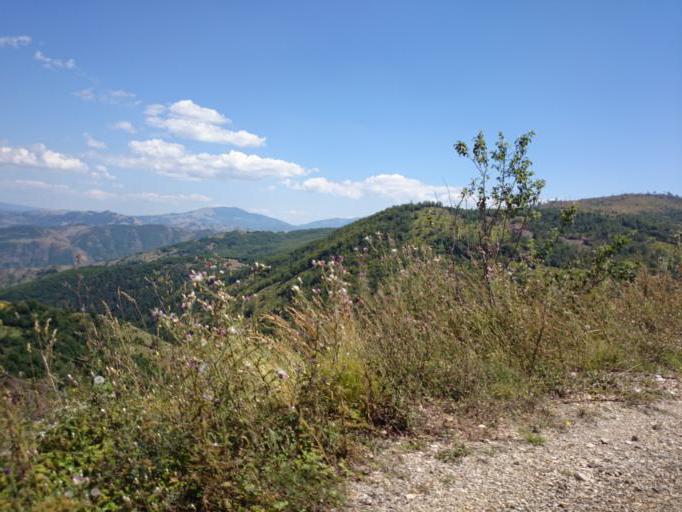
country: AL
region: Diber
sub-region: Rrethi i Bulqizes
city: Zerqan
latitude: 41.4308
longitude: 20.3289
